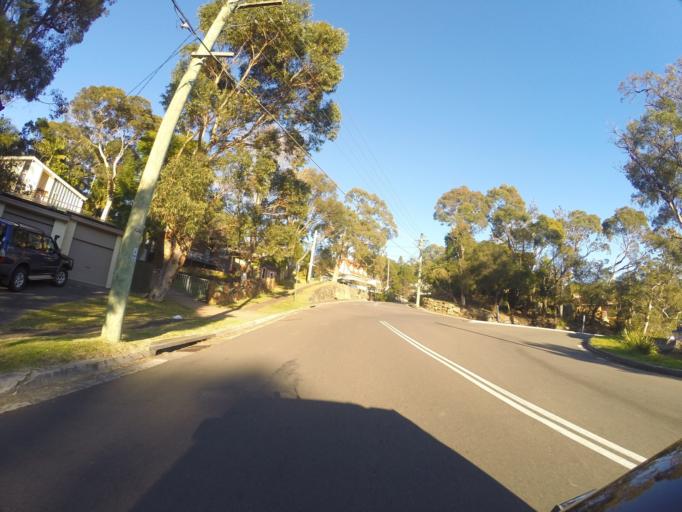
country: AU
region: New South Wales
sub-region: Sutherland Shire
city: Grays Point
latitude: -34.0583
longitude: 151.0766
